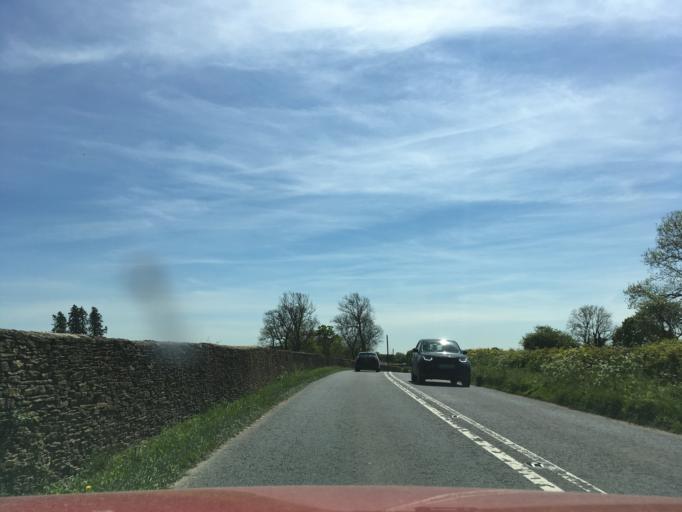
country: GB
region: England
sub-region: Wiltshire
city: Malmesbury
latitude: 51.6012
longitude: -2.0872
